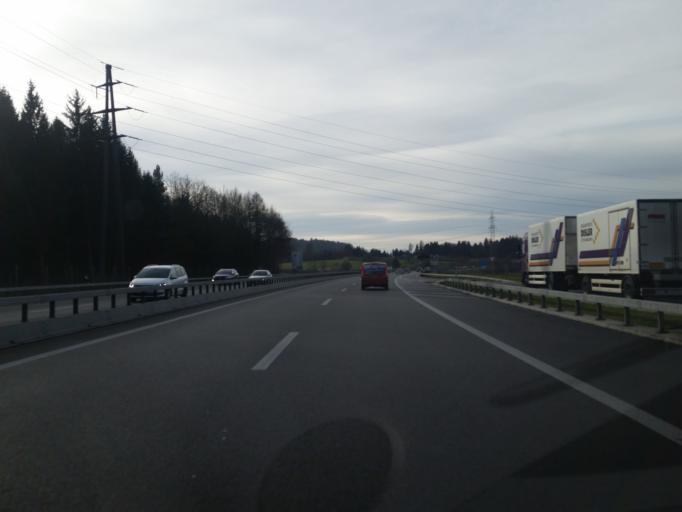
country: CH
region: Aargau
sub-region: Bezirk Brugg
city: Birr
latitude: 47.4291
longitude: 8.2368
